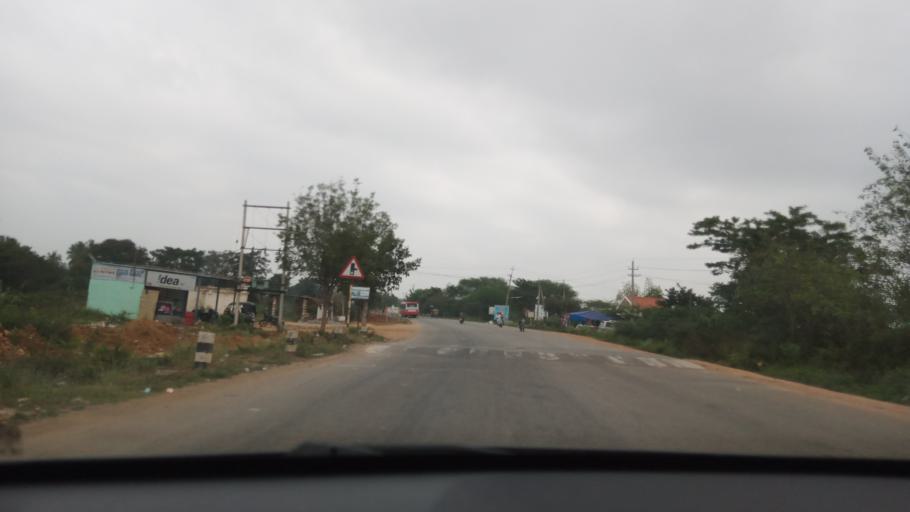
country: IN
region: Karnataka
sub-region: Bangalore Rural
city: Vijayapura
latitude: 13.2503
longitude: 77.9375
